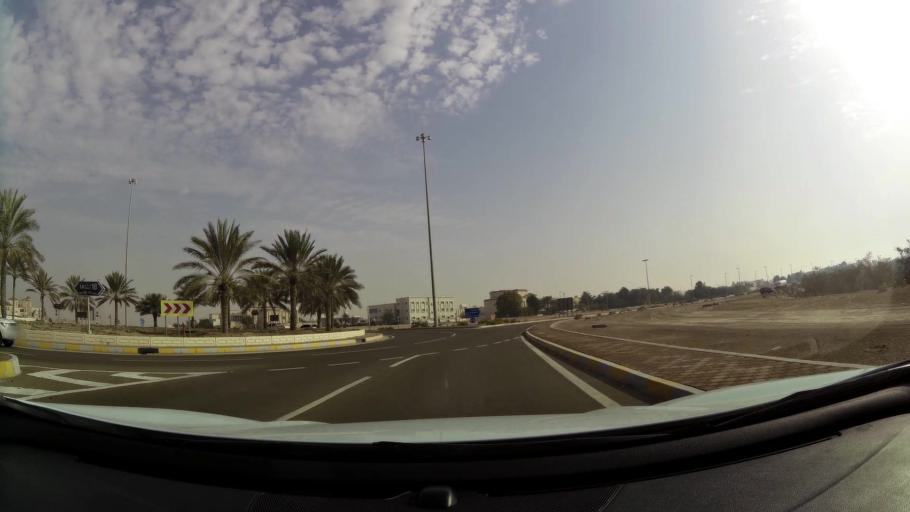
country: AE
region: Abu Dhabi
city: Abu Dhabi
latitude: 24.2554
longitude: 54.7105
